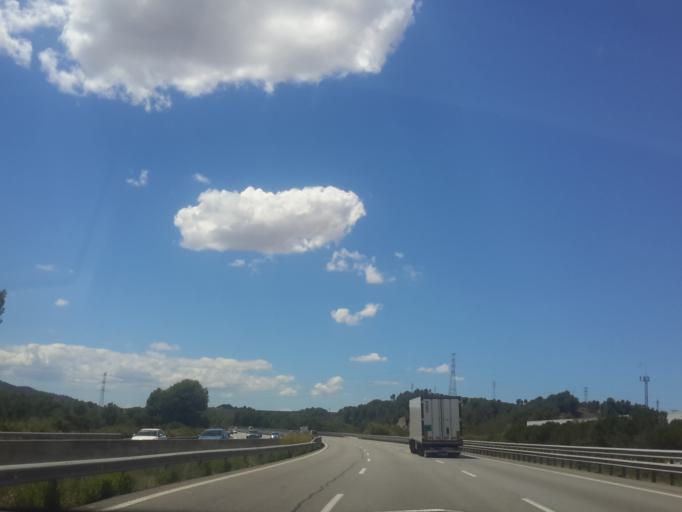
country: ES
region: Catalonia
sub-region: Provincia de Barcelona
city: Gelida
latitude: 41.4428
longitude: 1.8499
